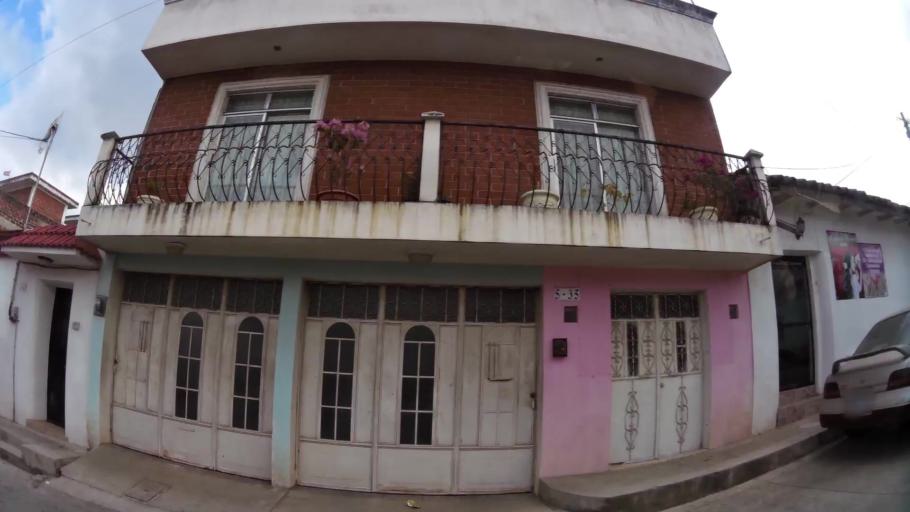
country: GT
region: Quetzaltenango
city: Salcaja
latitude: 14.8791
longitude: -91.4534
